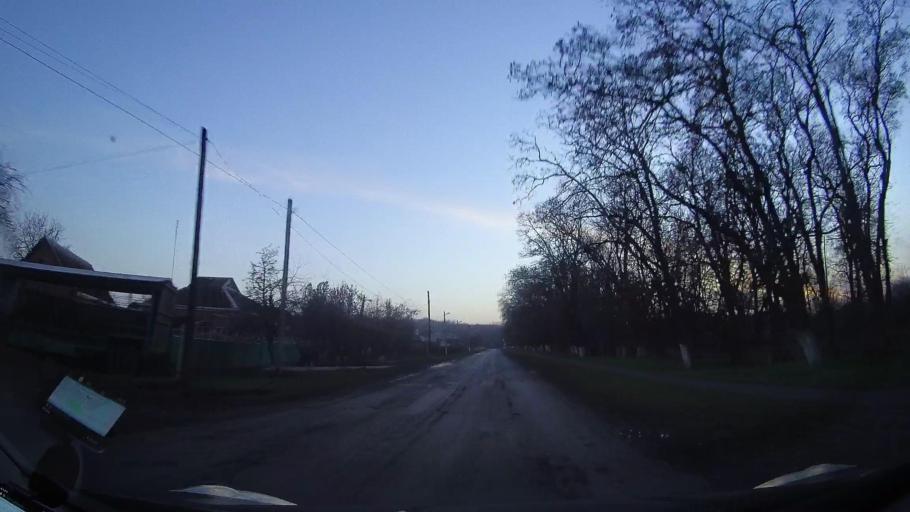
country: RU
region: Rostov
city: Zernograd
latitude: 46.8597
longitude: 40.3217
